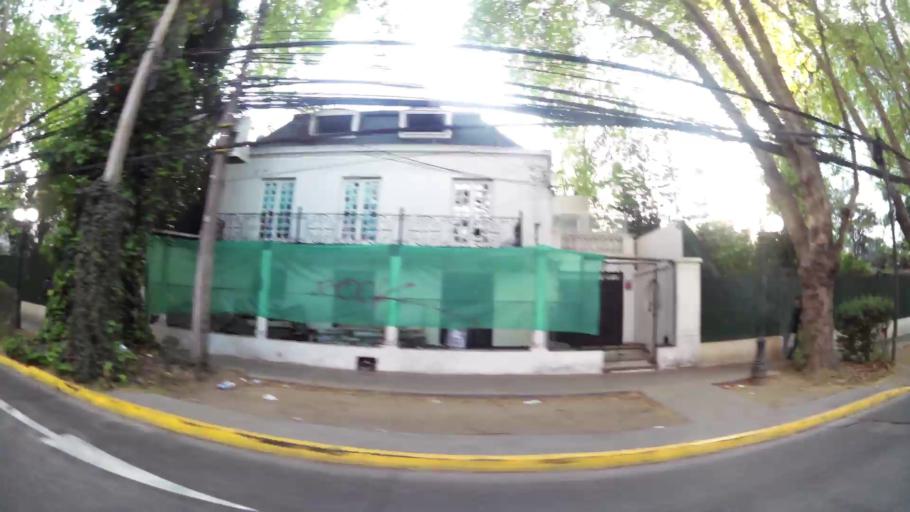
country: CL
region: Santiago Metropolitan
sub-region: Provincia de Santiago
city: Santiago
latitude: -33.4236
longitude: -70.6169
